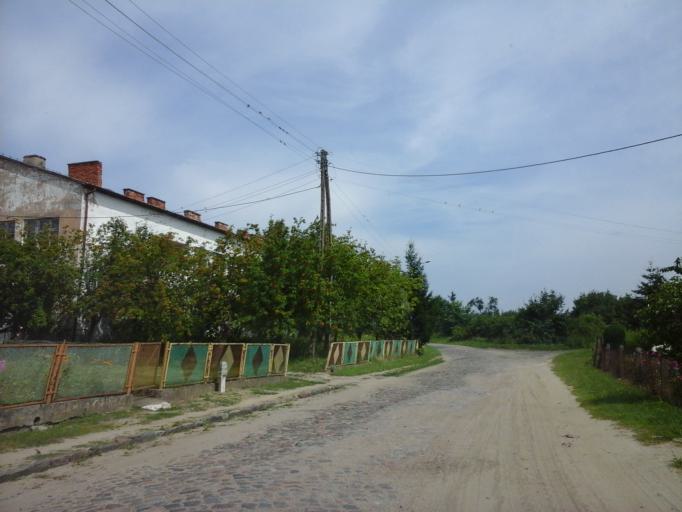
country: PL
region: West Pomeranian Voivodeship
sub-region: Powiat choszczenski
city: Bierzwnik
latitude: 52.9931
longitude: 15.6334
